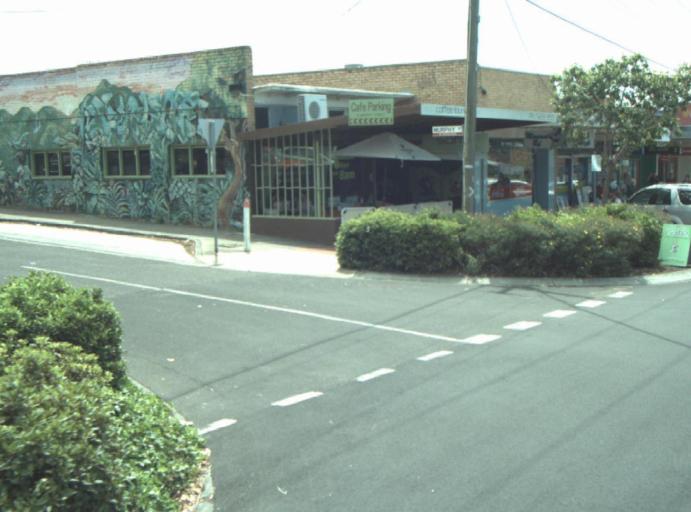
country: AU
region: Victoria
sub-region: Greater Geelong
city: Hamlyn Heights
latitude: -38.1310
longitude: 144.3317
